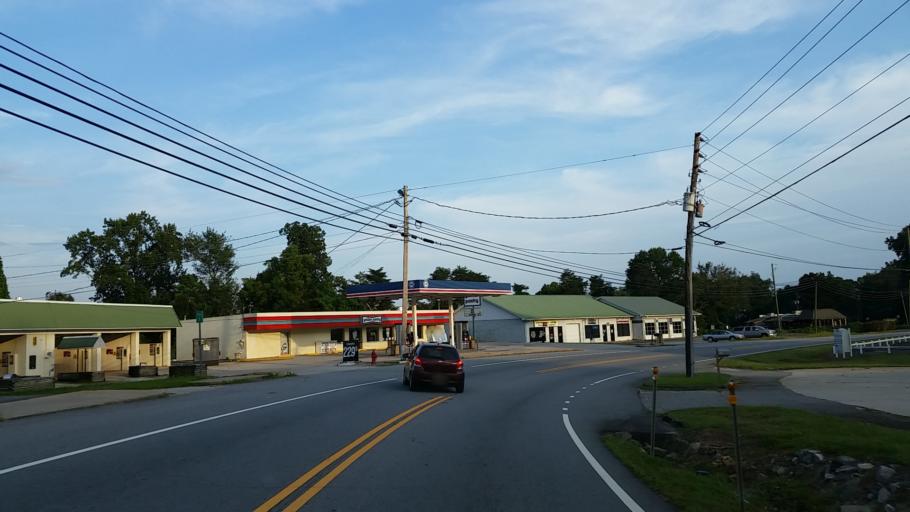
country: US
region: Georgia
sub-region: Lumpkin County
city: Dahlonega
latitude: 34.5400
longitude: -83.9873
